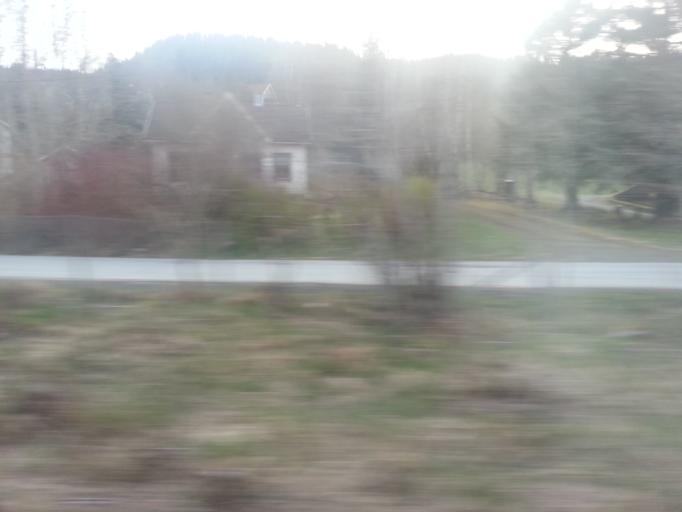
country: NO
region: Sor-Trondelag
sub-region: Melhus
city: Melhus
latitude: 63.2321
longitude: 10.2814
